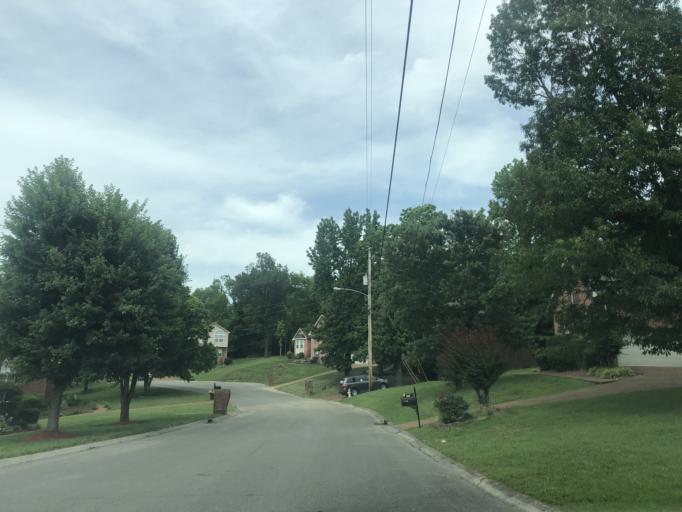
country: US
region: Tennessee
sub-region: Davidson County
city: Nashville
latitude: 36.2113
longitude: -86.8087
